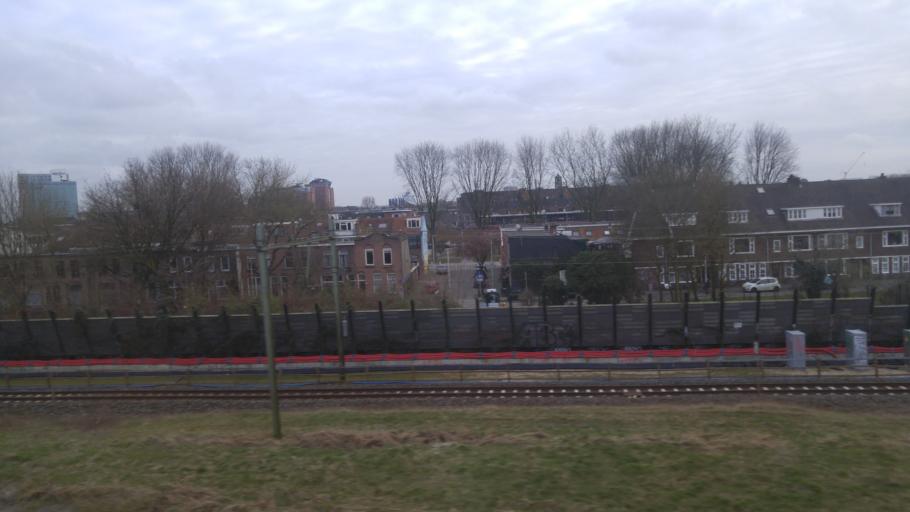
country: NL
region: Utrecht
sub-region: Gemeente Utrecht
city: Utrecht
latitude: 52.0965
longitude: 5.0998
